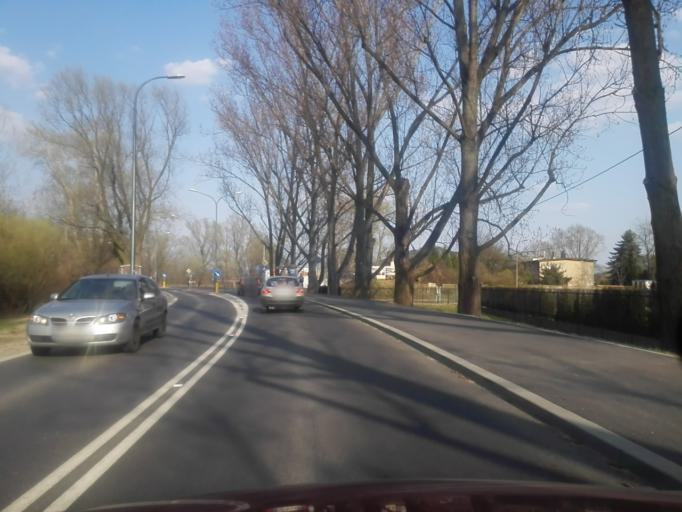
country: PL
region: Masovian Voivodeship
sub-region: Warszawa
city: Wilanow
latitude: 52.1611
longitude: 21.1040
